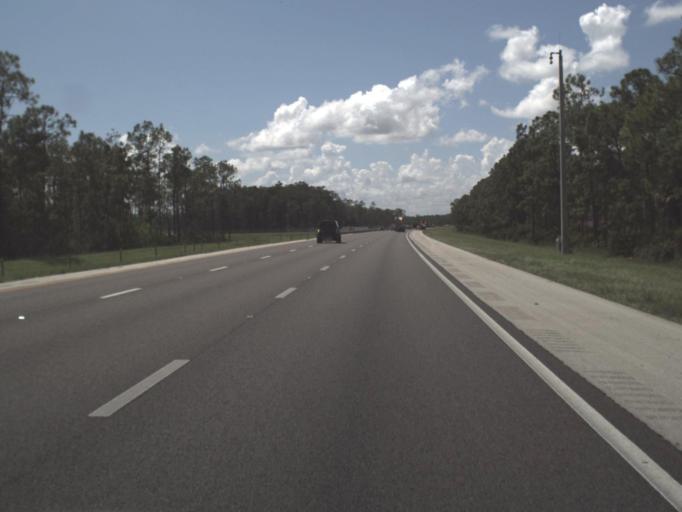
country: US
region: Florida
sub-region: Lee County
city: Gateway
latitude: 26.5809
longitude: -81.7945
